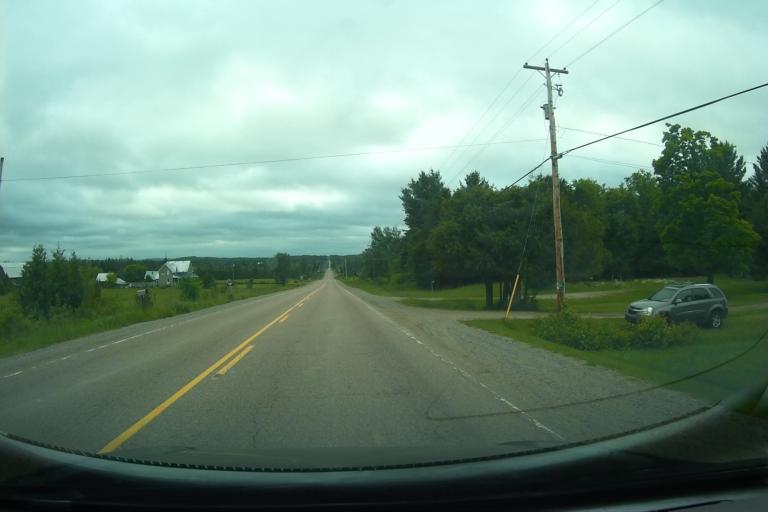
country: CA
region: Ontario
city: Pembroke
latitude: 45.5296
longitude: -77.1062
